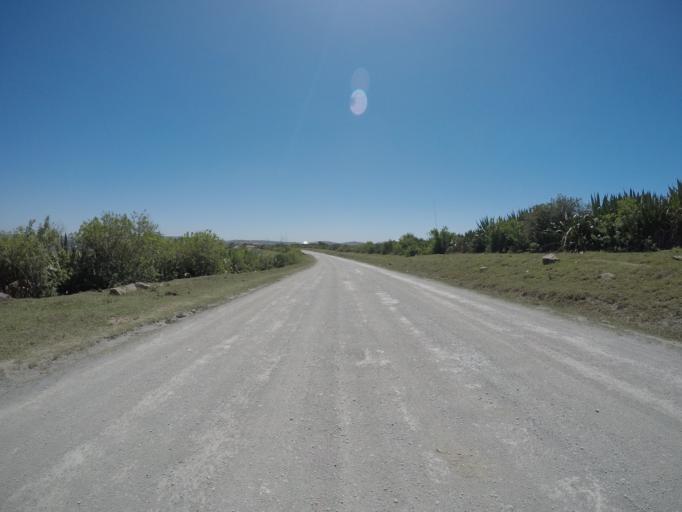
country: ZA
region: Eastern Cape
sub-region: OR Tambo District Municipality
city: Libode
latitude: -32.0086
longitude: 29.0736
